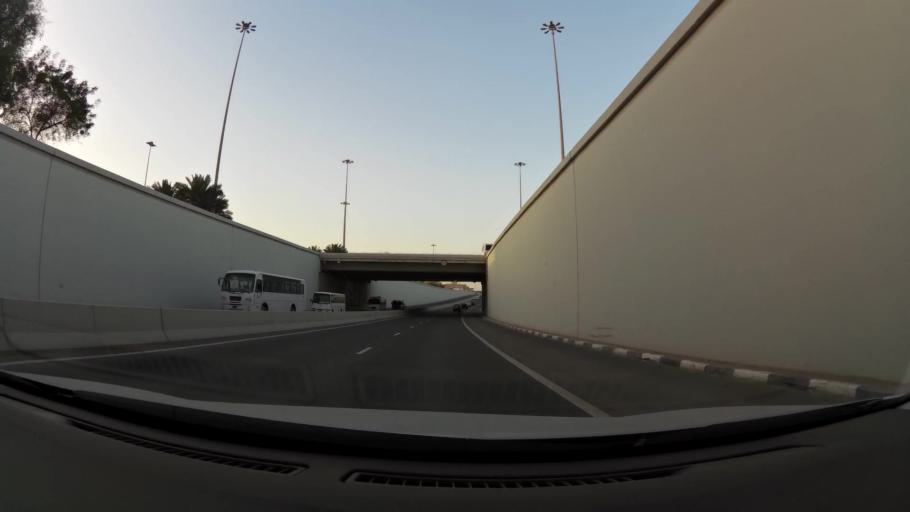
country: QA
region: Baladiyat ar Rayyan
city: Ar Rayyan
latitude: 25.3195
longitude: 51.4602
